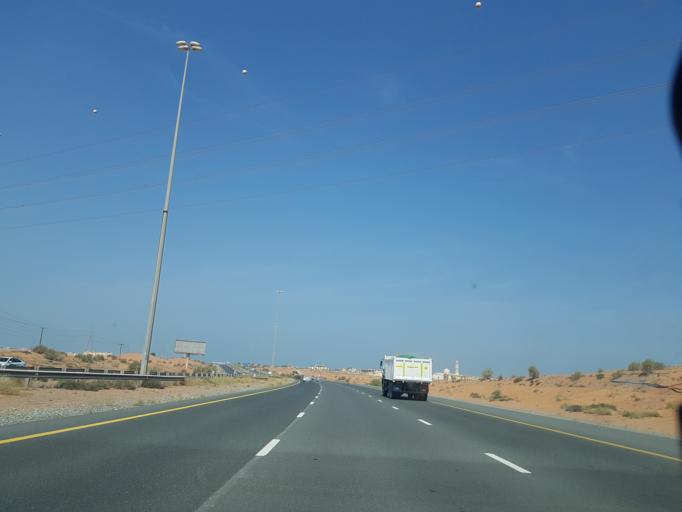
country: AE
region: Ra's al Khaymah
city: Ras al-Khaimah
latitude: 25.6842
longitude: 55.8830
